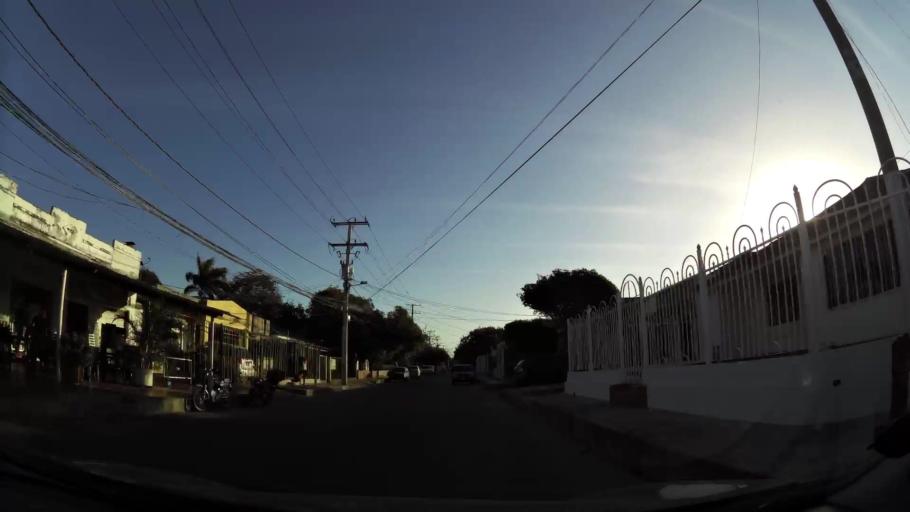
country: CO
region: Atlantico
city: Barranquilla
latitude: 10.9704
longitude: -74.7949
